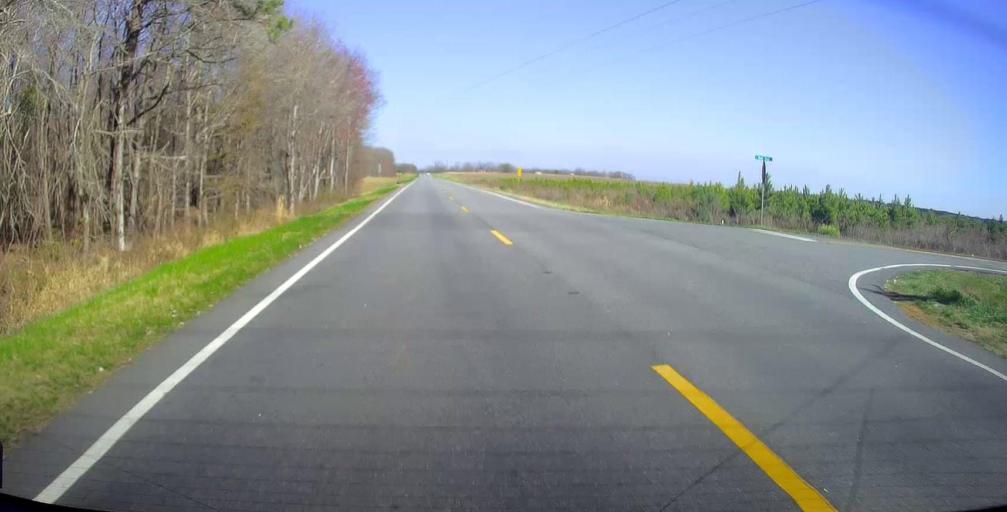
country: US
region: Georgia
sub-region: Dooly County
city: Unadilla
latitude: 32.3378
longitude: -83.8282
